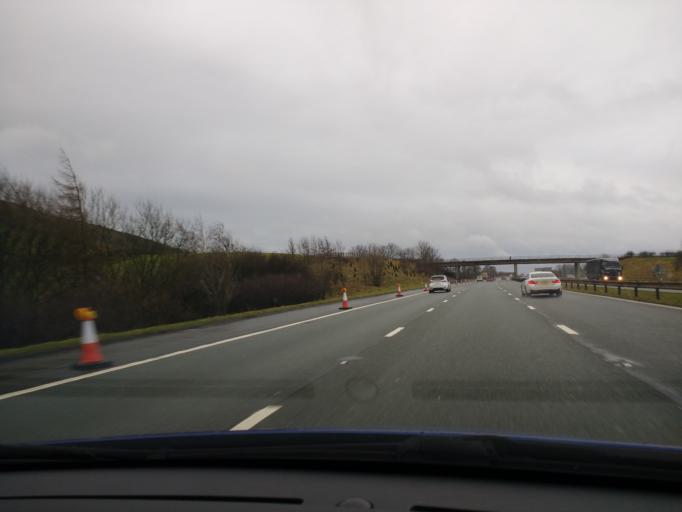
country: GB
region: England
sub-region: Cumbria
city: Milnthorpe
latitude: 54.2220
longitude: -2.7208
